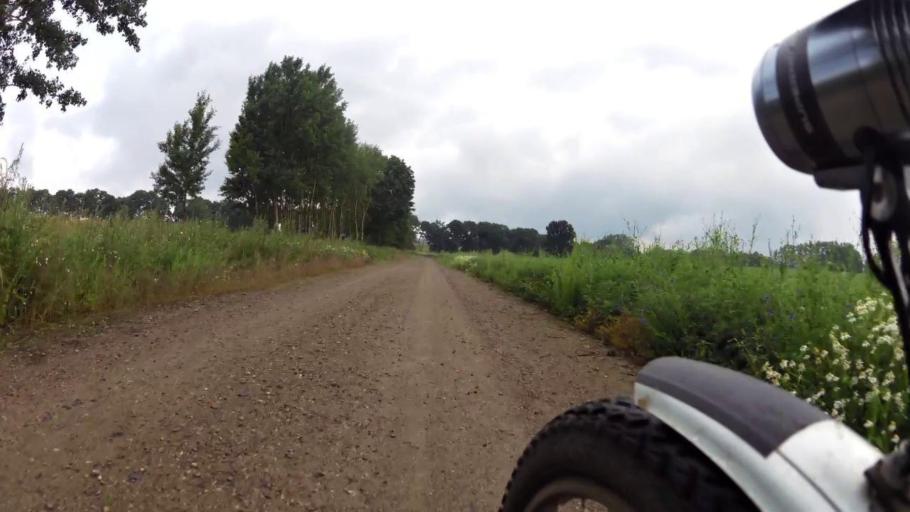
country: PL
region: West Pomeranian Voivodeship
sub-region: Powiat lobeski
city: Lobez
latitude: 53.7244
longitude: 15.6327
